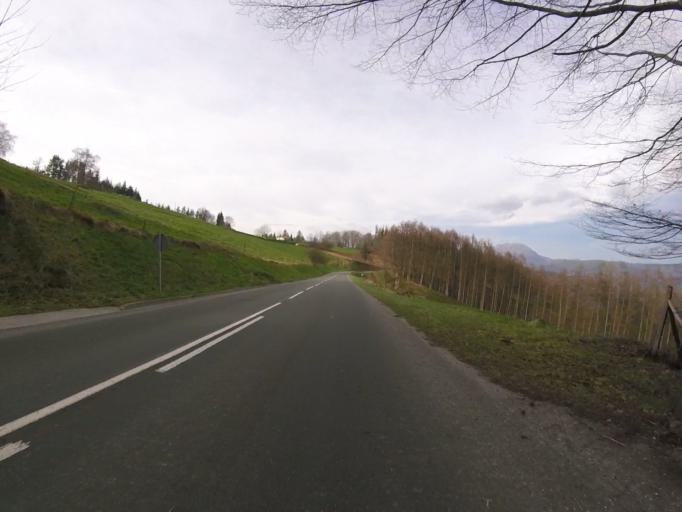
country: ES
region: Basque Country
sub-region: Provincia de Guipuzcoa
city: Beizama
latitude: 43.1526
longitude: -2.1953
